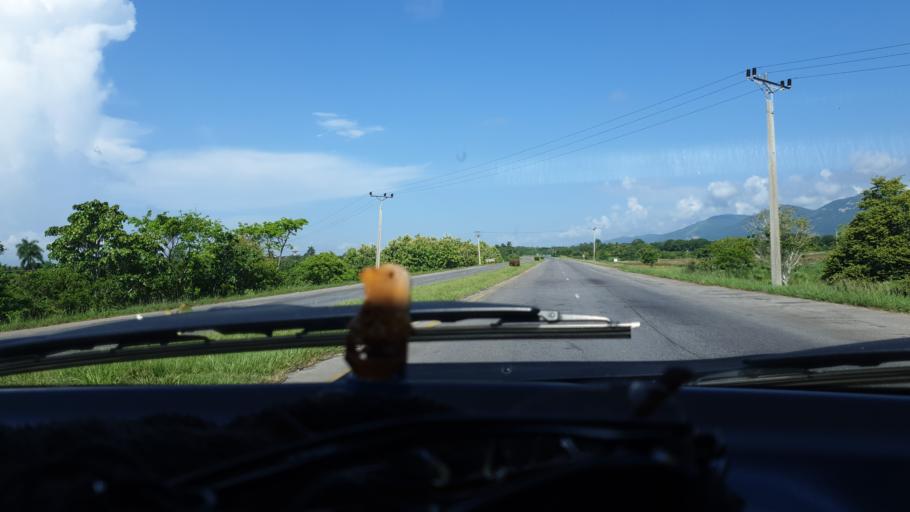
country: CU
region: Artemisa
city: San Cristobal
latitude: 22.7219
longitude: -83.0432
